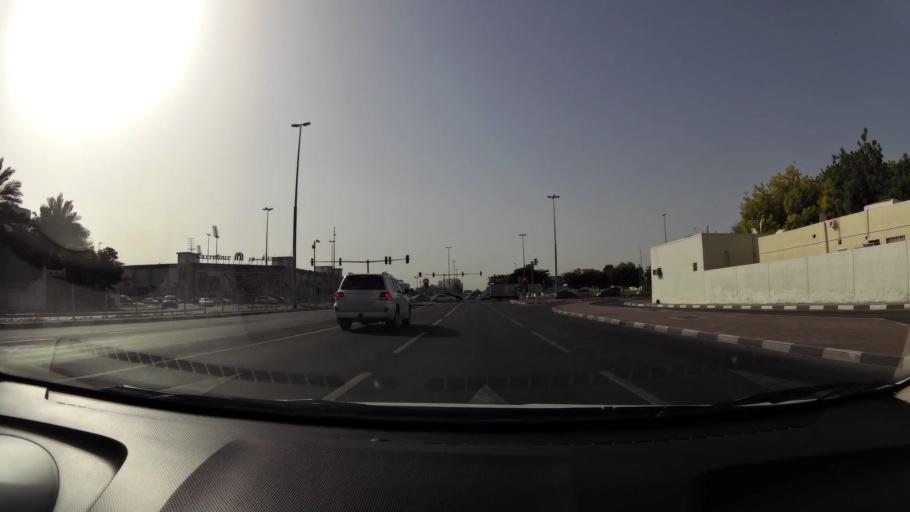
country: AE
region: Ash Shariqah
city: Sharjah
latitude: 25.2908
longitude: 55.3447
